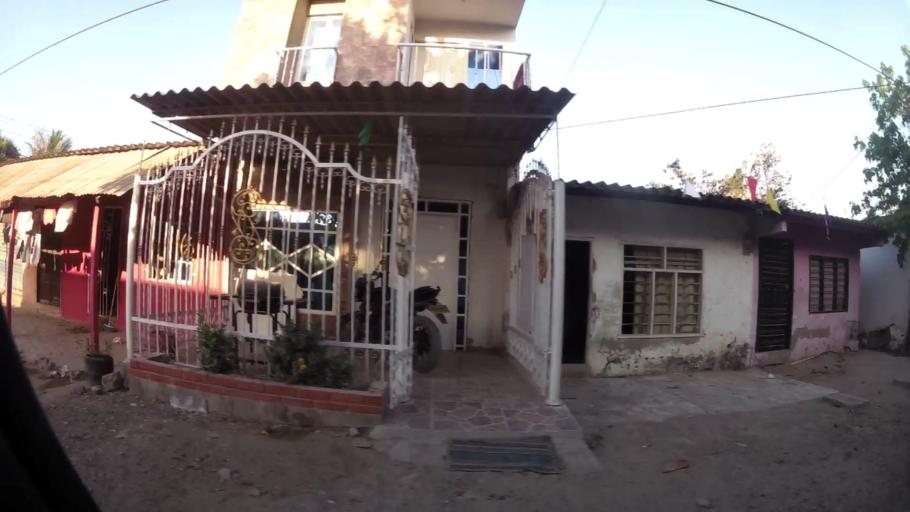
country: CO
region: Bolivar
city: Cartagena
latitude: 10.4076
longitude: -75.4531
